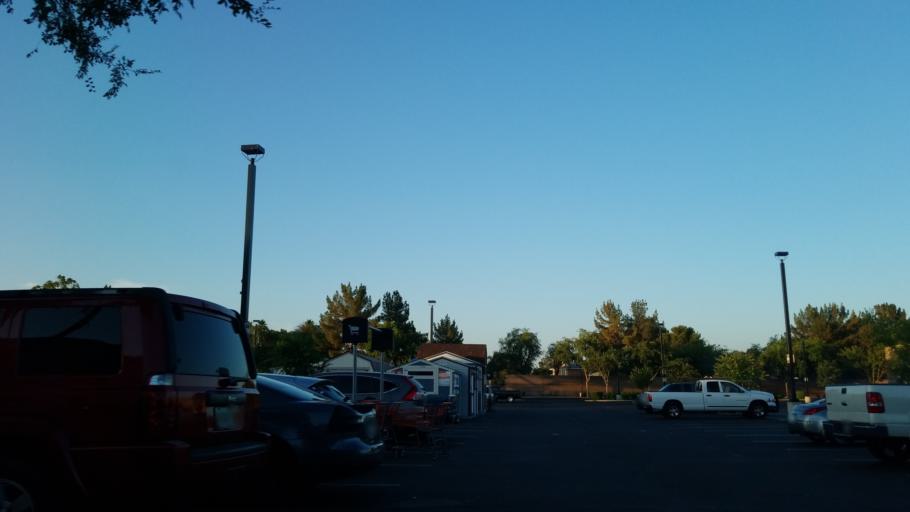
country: US
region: Arizona
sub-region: Maricopa County
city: Glendale
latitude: 33.6123
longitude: -112.1139
